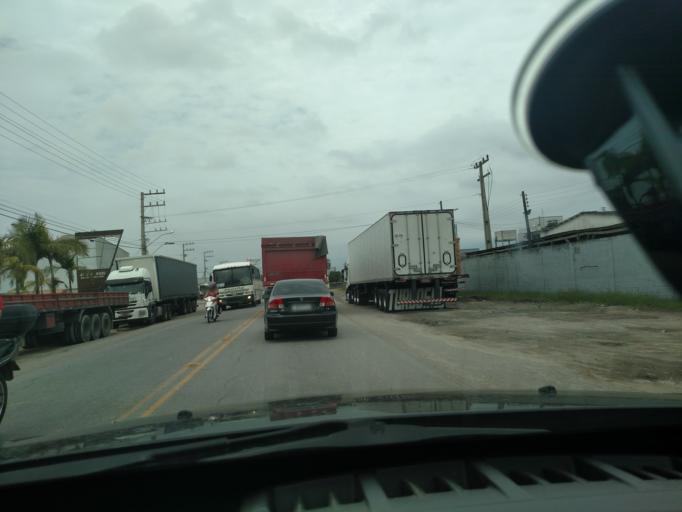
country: BR
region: Santa Catarina
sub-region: Itajai
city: Itajai
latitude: -26.8875
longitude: -48.7344
